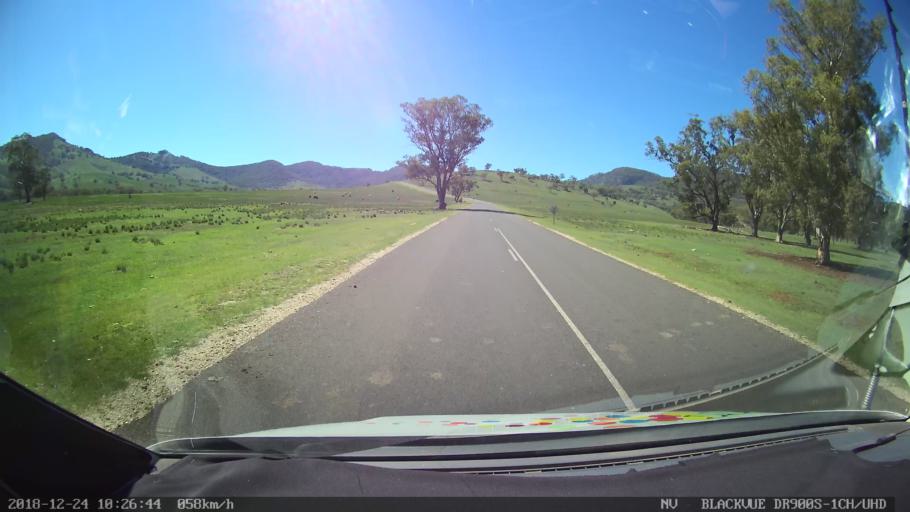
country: AU
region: New South Wales
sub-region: Liverpool Plains
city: Quirindi
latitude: -31.8124
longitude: 150.5275
